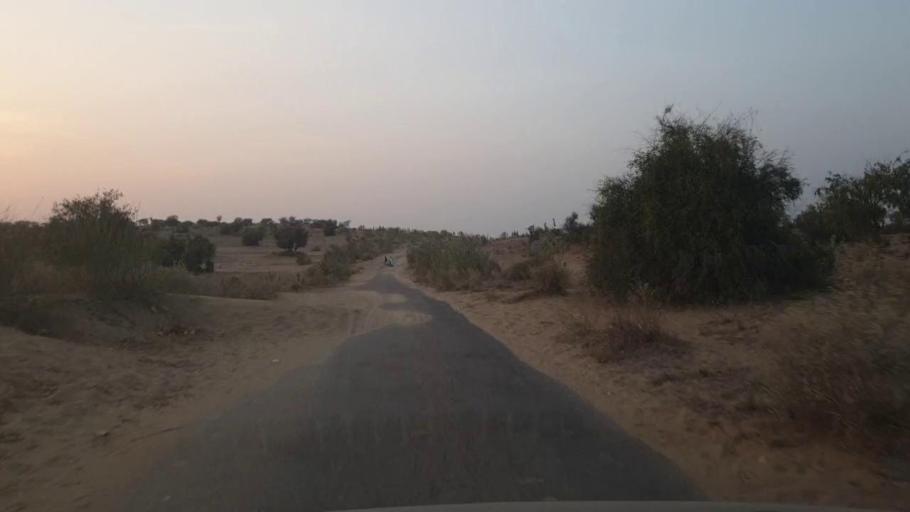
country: PK
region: Sindh
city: Umarkot
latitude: 25.3401
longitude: 70.0529
